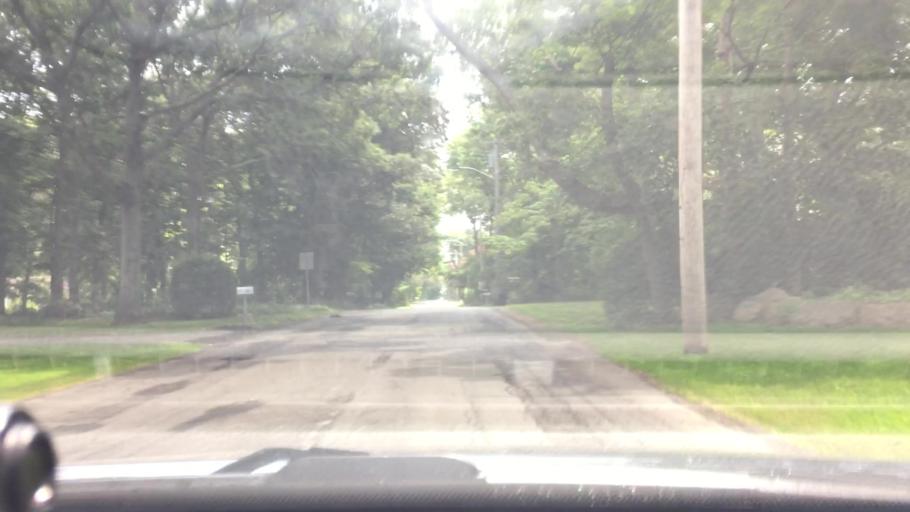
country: US
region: New York
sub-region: Suffolk County
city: Mount Sinai
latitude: 40.9285
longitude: -73.0154
